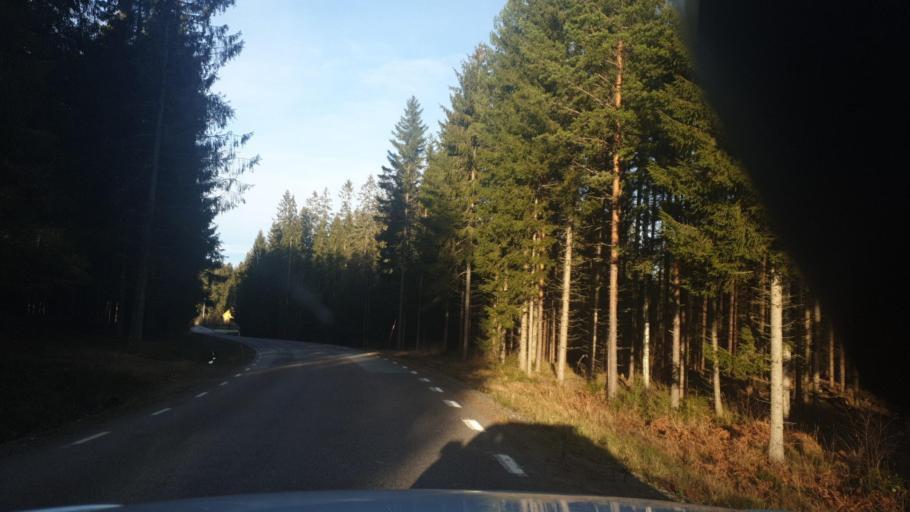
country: SE
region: Vaermland
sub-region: Grums Kommun
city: Grums
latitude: 59.4979
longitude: 12.8776
